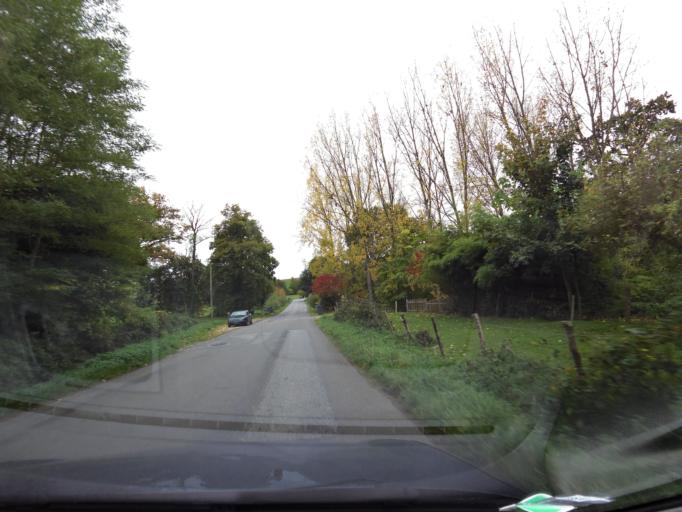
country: FR
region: Brittany
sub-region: Departement d'Ille-et-Vilaine
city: Corps-Nuds
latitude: 47.9735
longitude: -1.5904
